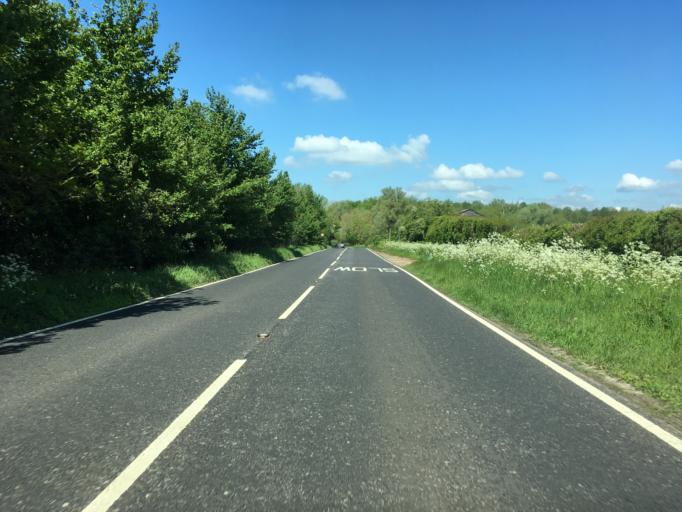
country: GB
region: England
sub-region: Buckinghamshire
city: Buckingham
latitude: 52.0030
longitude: -1.0029
